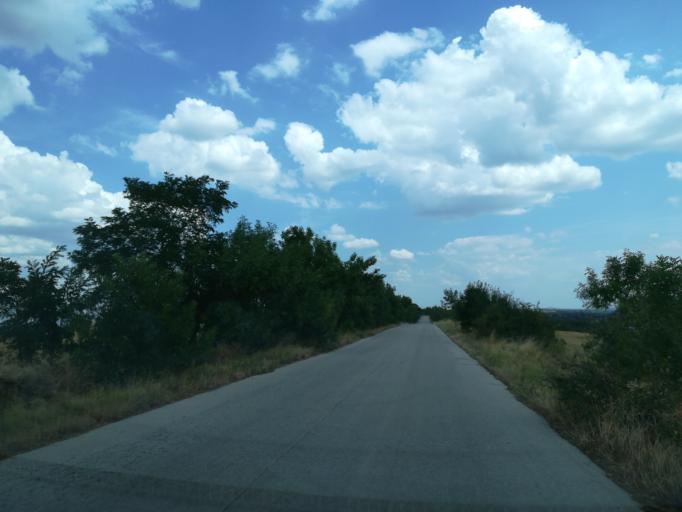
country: BG
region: Khaskovo
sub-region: Obshtina Mineralni Bani
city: Mineralni Bani
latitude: 41.9764
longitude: 25.1523
